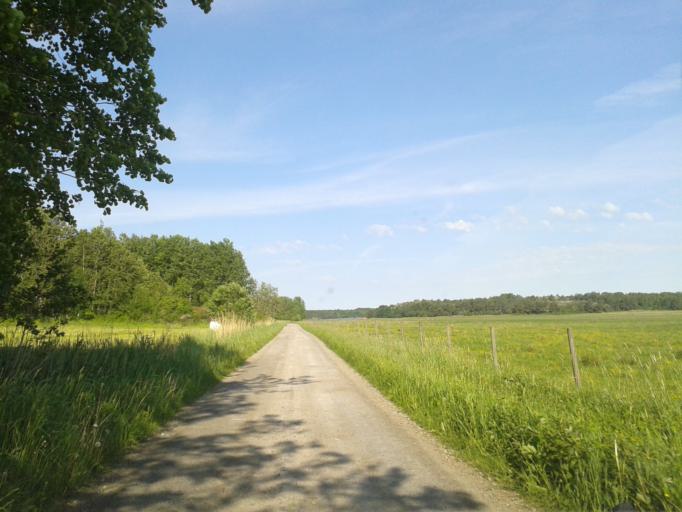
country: SE
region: Vaestra Goetaland
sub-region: Stromstads Kommun
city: Stroemstad
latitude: 58.8626
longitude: 11.2184
